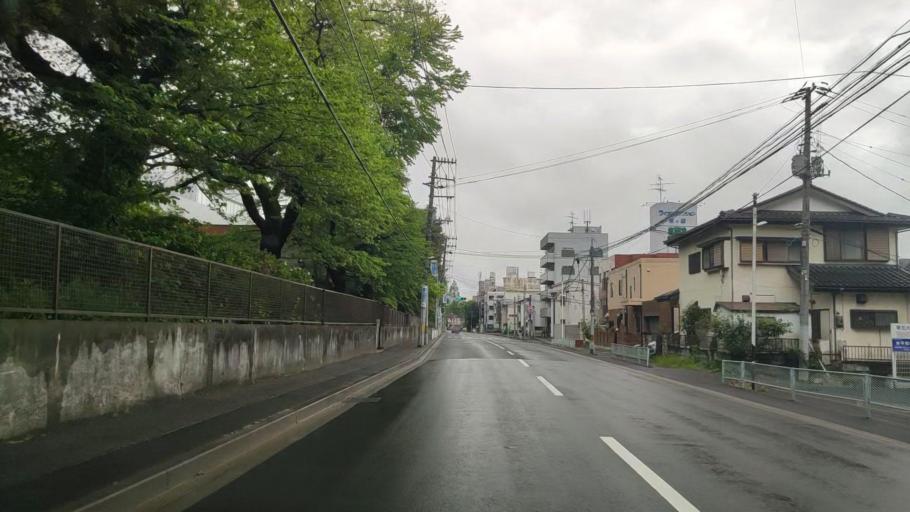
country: JP
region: Miyagi
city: Sendai
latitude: 38.2527
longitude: 140.8725
